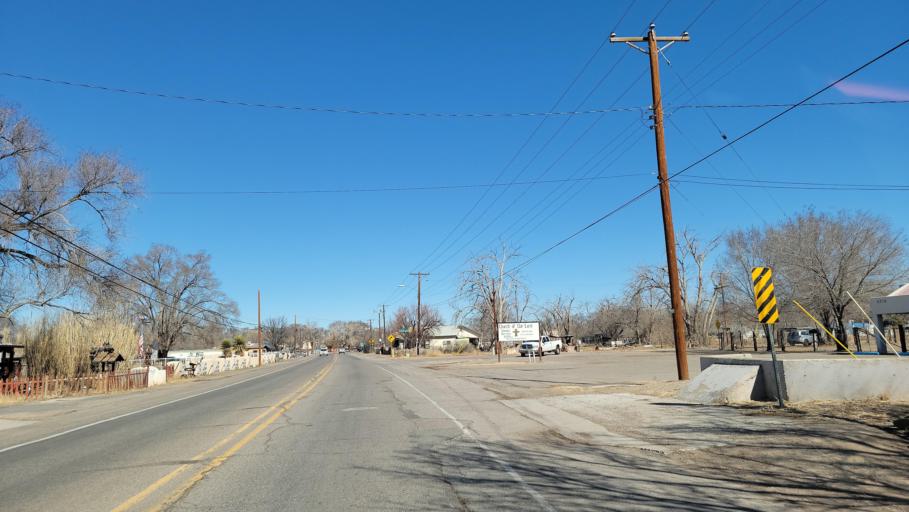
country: US
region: New Mexico
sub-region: Bernalillo County
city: South Valley
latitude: 34.9845
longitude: -106.6968
